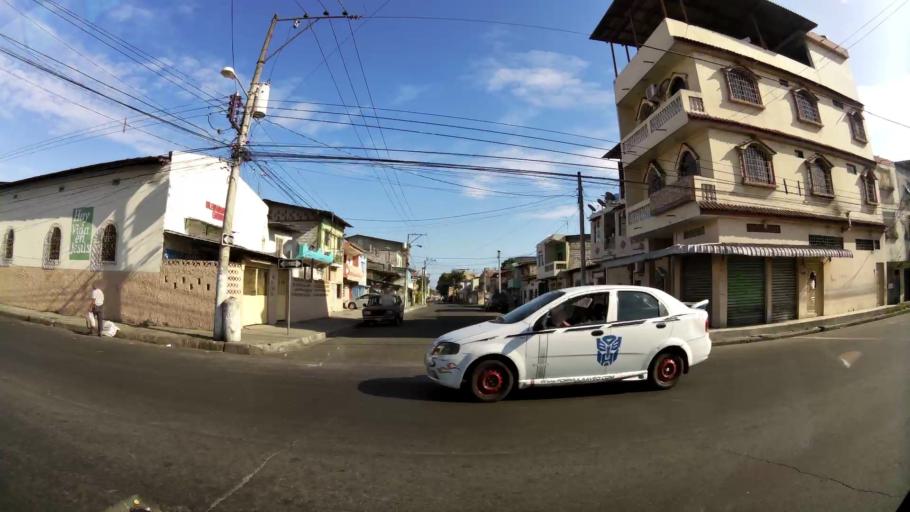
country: EC
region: Guayas
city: Guayaquil
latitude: -2.2036
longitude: -79.9218
